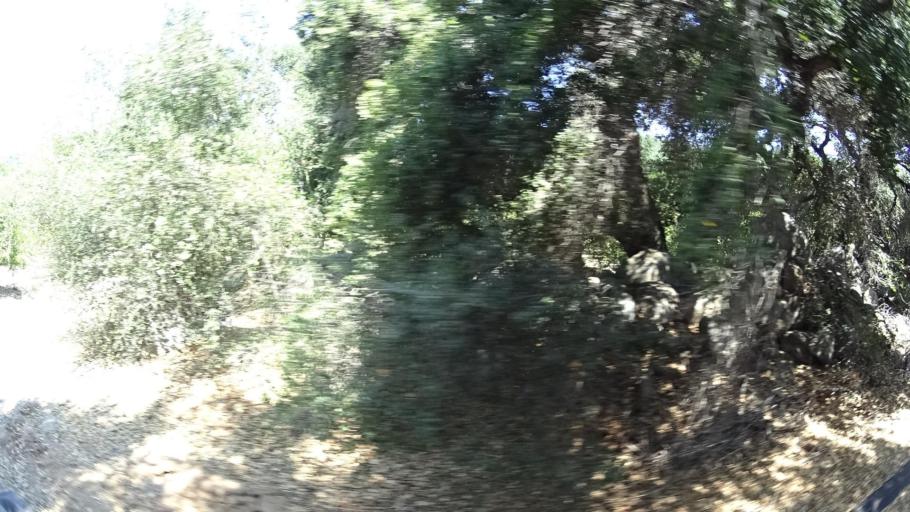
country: US
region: California
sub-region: San Diego County
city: Valley Center
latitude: 33.2920
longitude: -116.9567
